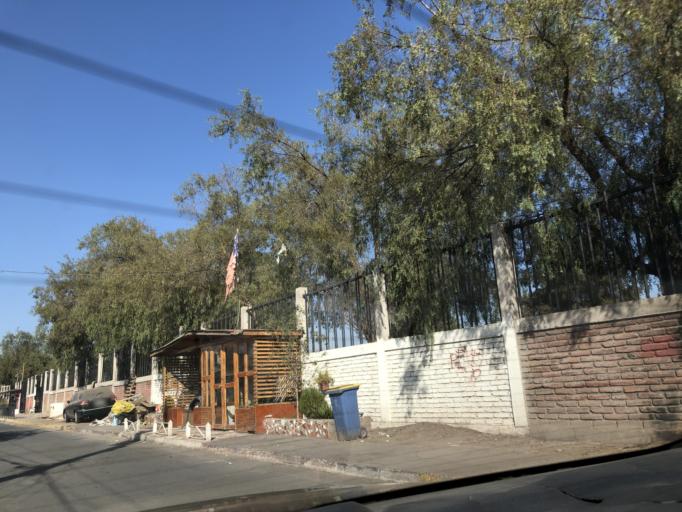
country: CL
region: Santiago Metropolitan
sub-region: Provincia de Santiago
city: La Pintana
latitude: -33.5682
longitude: -70.6115
